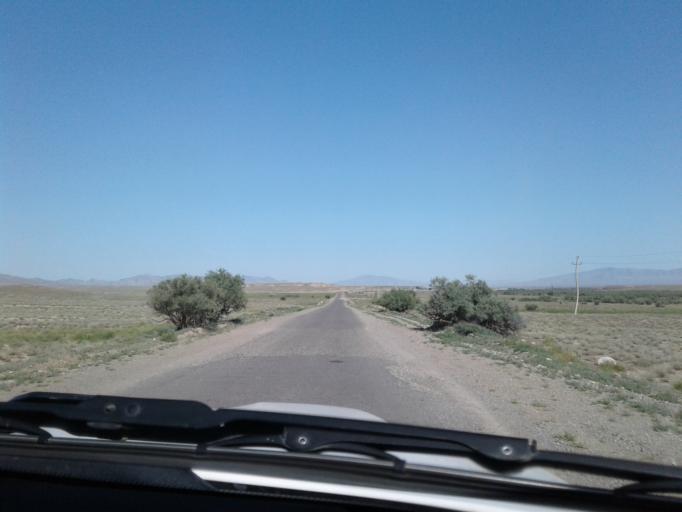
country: TM
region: Balkan
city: Serdar
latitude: 38.7206
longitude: 56.3022
